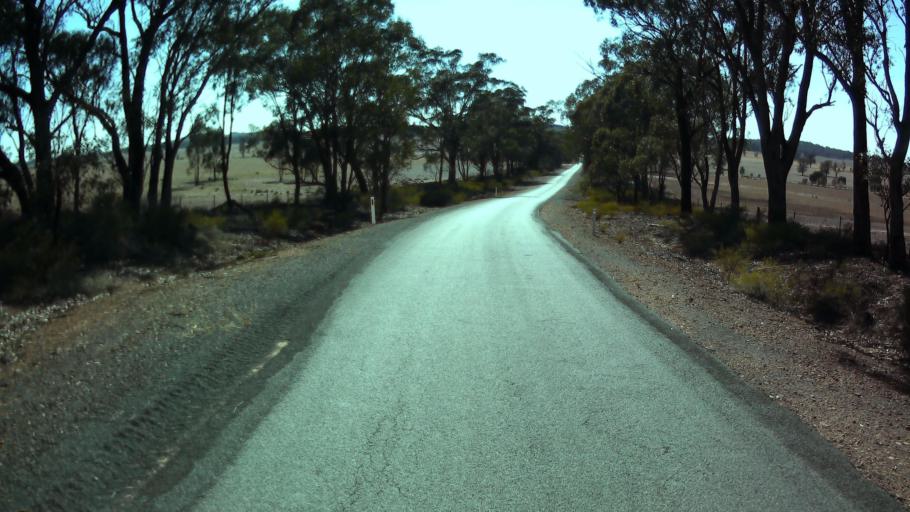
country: AU
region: New South Wales
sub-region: Weddin
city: Grenfell
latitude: -33.7821
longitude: 147.9632
